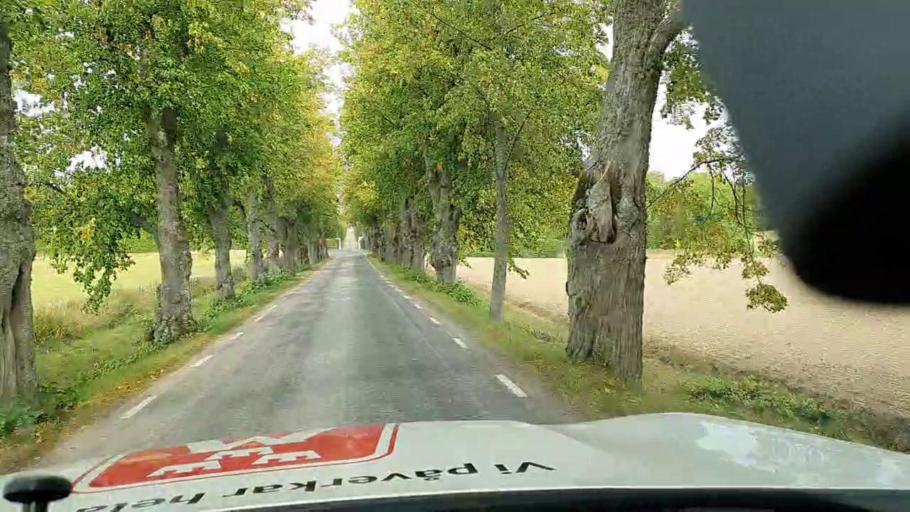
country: SE
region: Soedermanland
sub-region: Nykopings Kommun
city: Svalsta
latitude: 58.8222
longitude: 16.8933
